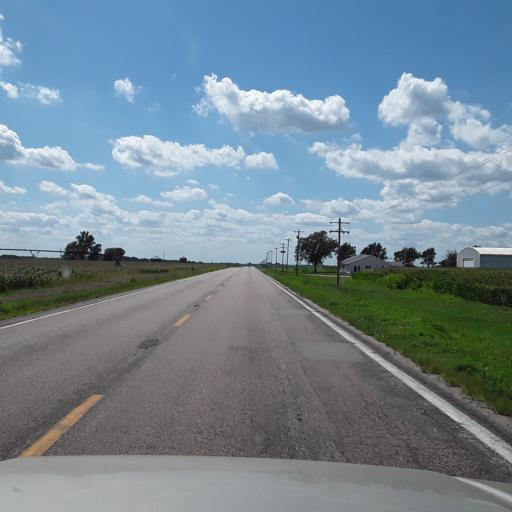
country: US
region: Nebraska
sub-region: Merrick County
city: Central City
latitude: 41.1911
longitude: -98.0332
